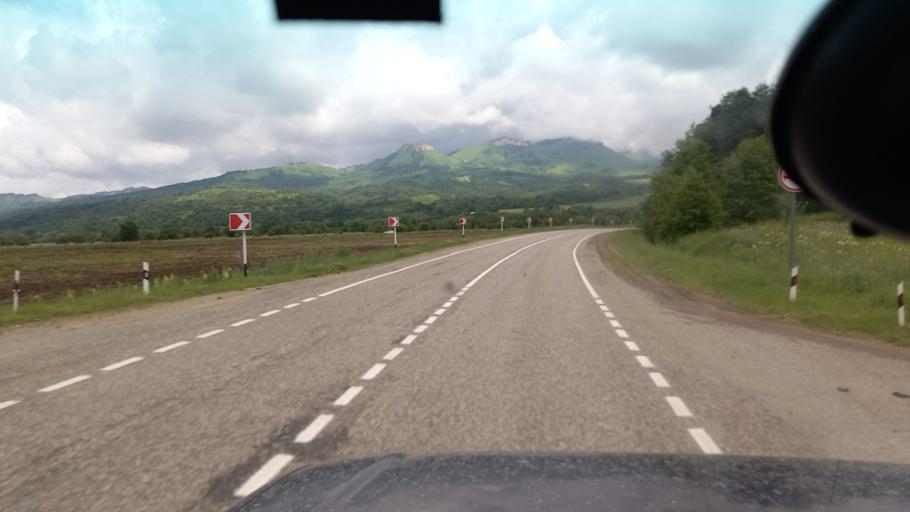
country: RU
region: Krasnodarskiy
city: Psebay
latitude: 44.1045
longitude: 40.8263
